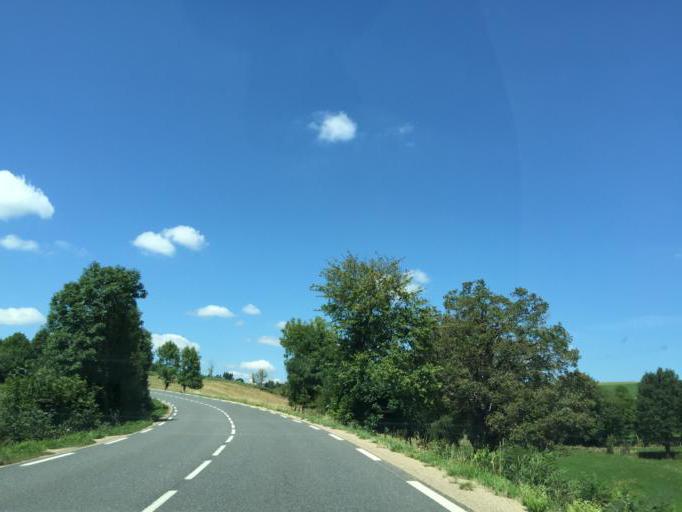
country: FR
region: Midi-Pyrenees
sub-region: Departement de l'Aveyron
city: Espalion
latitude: 44.5796
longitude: 2.7957
